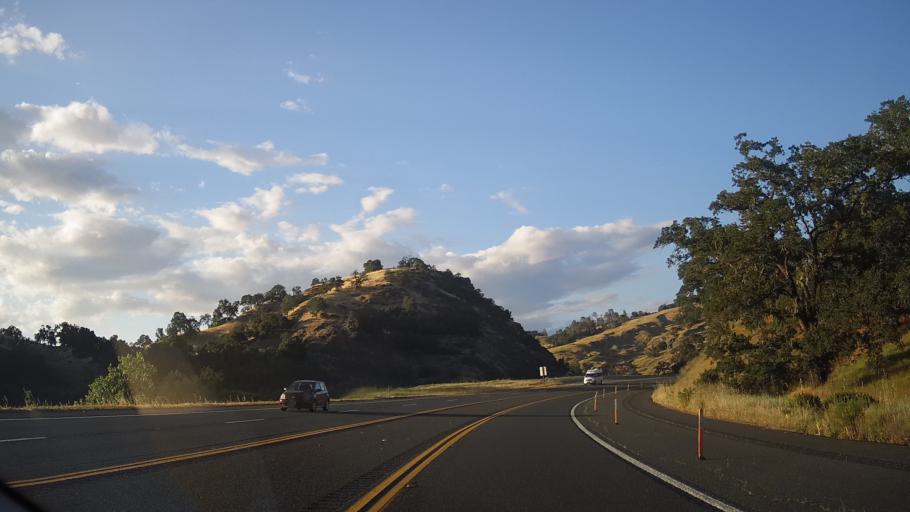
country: US
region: California
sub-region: Sonoma County
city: Cloverdale
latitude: 38.9053
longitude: -123.0567
